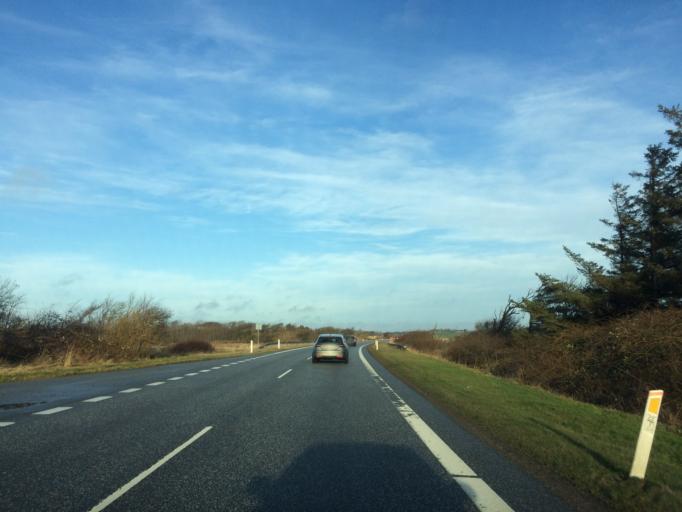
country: DK
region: North Denmark
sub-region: Thisted Kommune
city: Hurup
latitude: 56.8001
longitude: 8.4729
